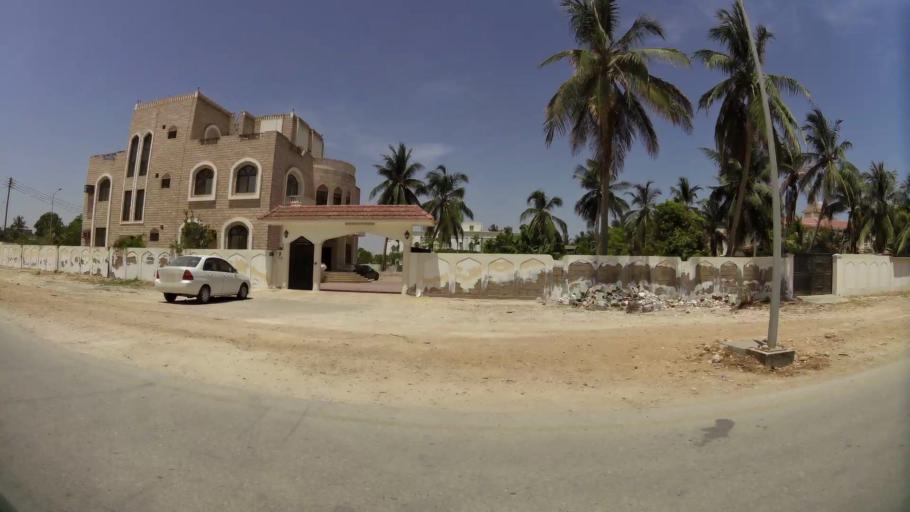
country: OM
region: Zufar
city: Salalah
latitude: 17.0623
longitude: 54.1512
